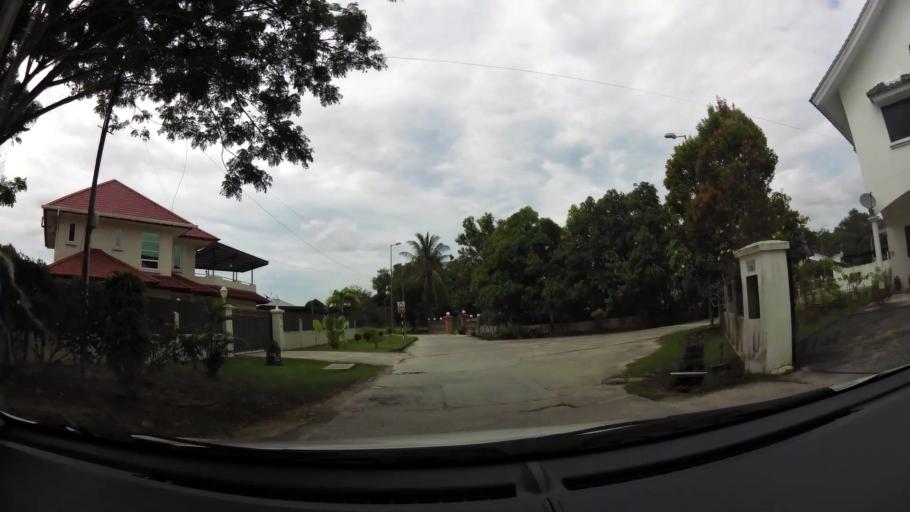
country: BN
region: Brunei and Muara
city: Bandar Seri Begawan
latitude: 4.8797
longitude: 114.8966
